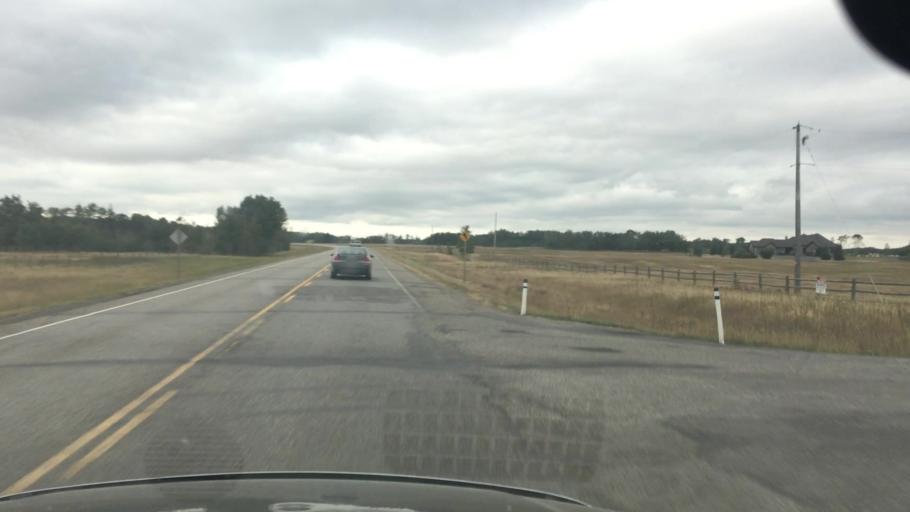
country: CA
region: Alberta
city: Cochrane
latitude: 51.3584
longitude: -114.4757
